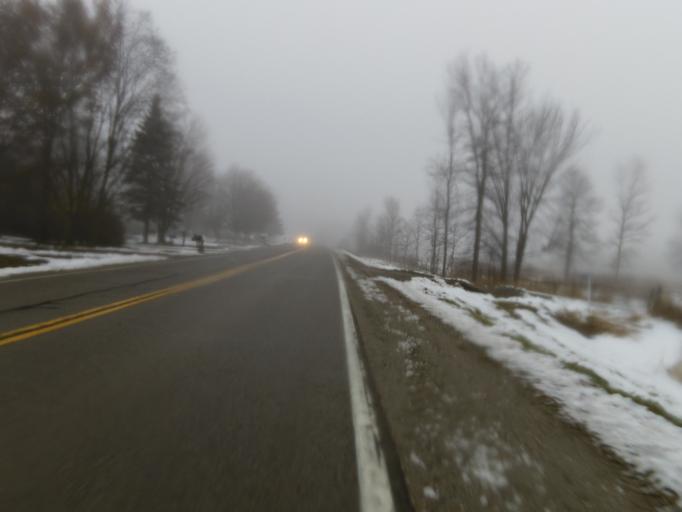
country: CA
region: Ontario
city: Perth
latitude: 44.8471
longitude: -76.3597
